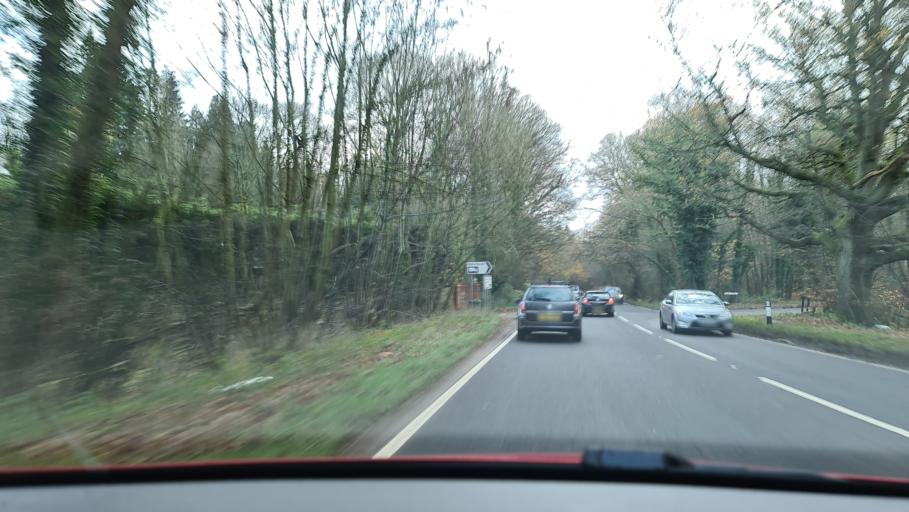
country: GB
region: England
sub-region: Buckinghamshire
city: Amersham
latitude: 51.6608
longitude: -0.6647
